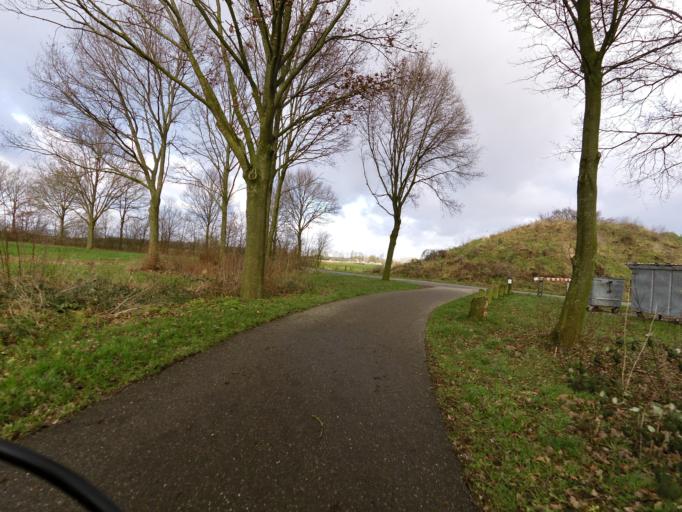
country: NL
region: Gelderland
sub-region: Gemeente Doetinchem
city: Doetinchem
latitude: 51.9382
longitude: 6.2720
